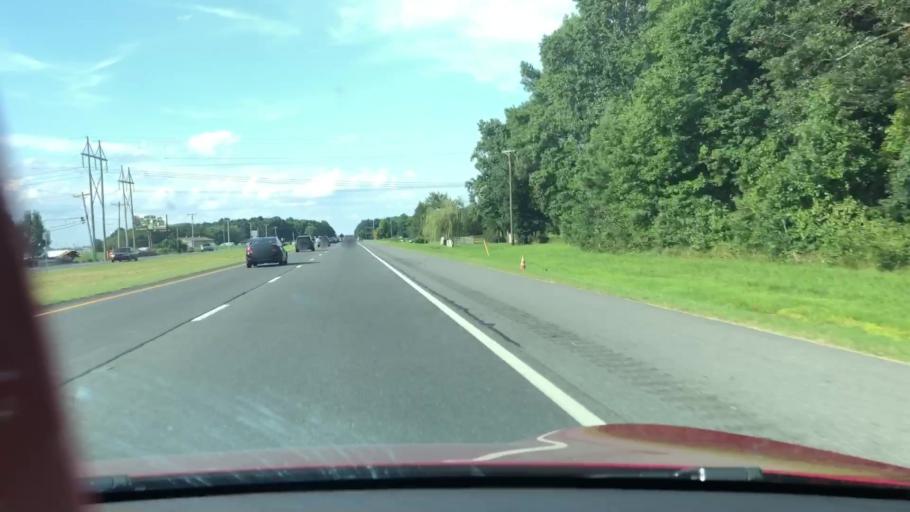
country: US
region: Delaware
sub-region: Kent County
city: Harrington
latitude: 38.8909
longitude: -75.5719
